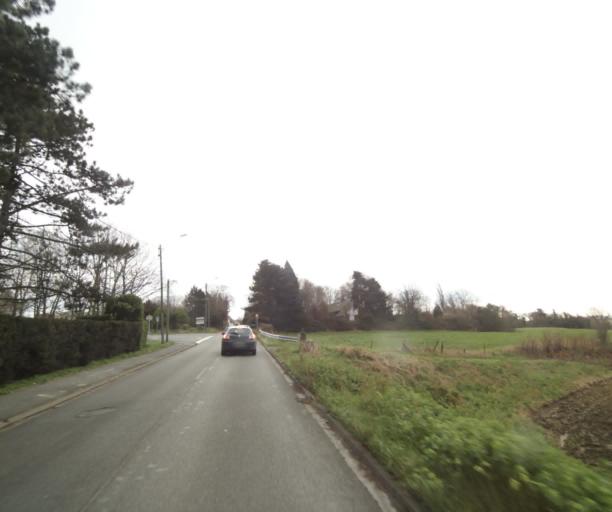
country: FR
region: Nord-Pas-de-Calais
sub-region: Departement du Nord
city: Saint-Saulve
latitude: 50.3624
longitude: 3.5462
